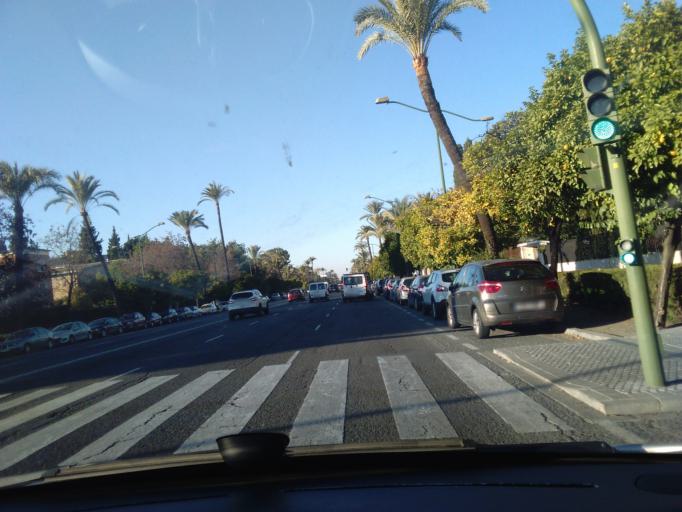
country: ES
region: Andalusia
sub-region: Provincia de Sevilla
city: Sevilla
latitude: 37.3617
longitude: -5.9832
